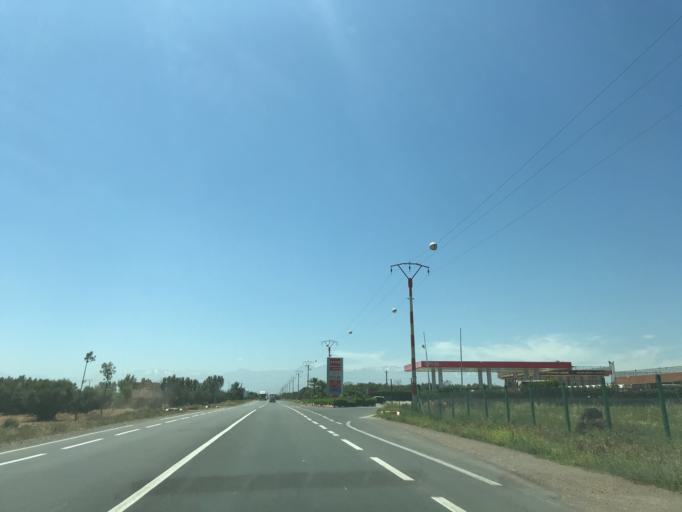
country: MA
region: Marrakech-Tensift-Al Haouz
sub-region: Marrakech
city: Marrakesh
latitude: 31.5454
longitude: -8.0034
